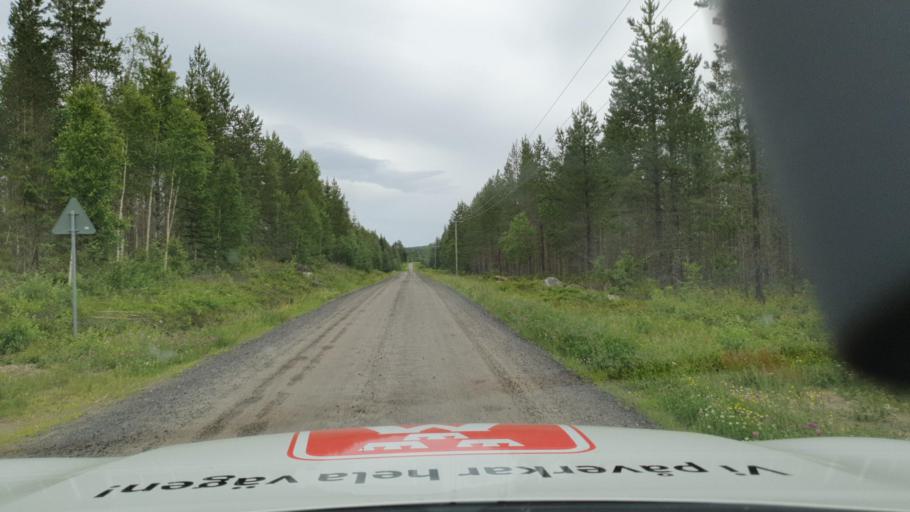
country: SE
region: Vaesterbotten
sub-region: Skelleftea Kommun
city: Burtraesk
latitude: 64.3439
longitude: 20.6025
